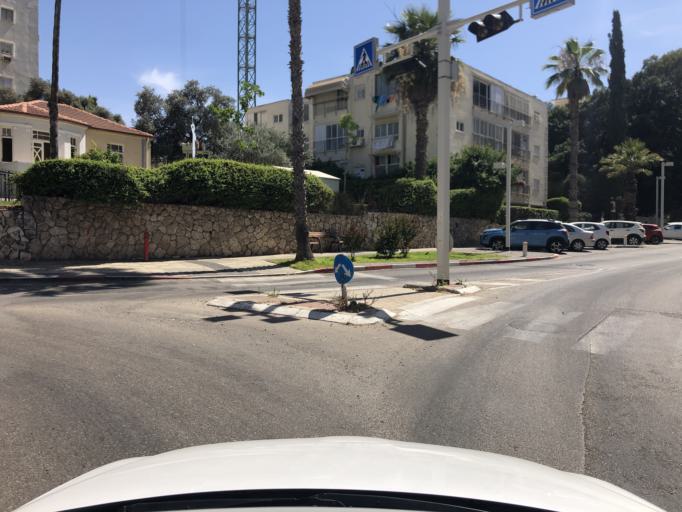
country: IL
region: Tel Aviv
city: Ramat Gan
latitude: 32.0782
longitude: 34.8041
